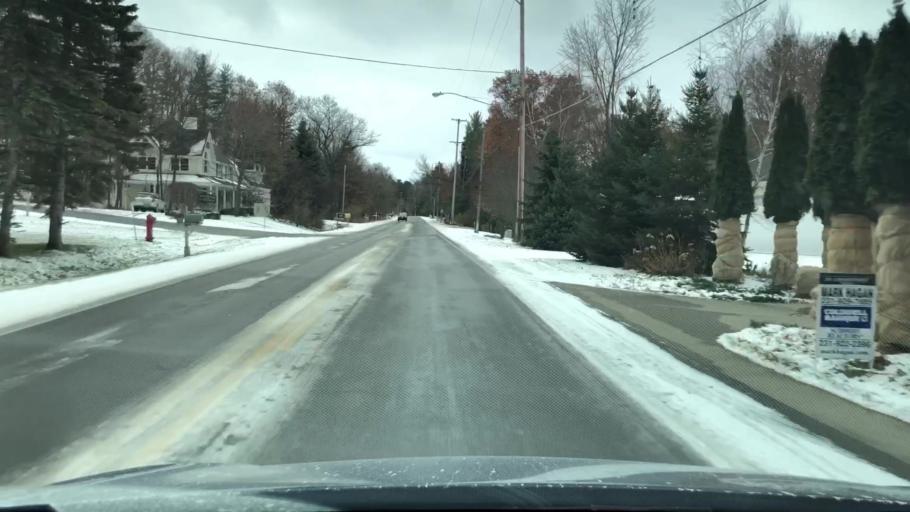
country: US
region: Michigan
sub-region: Grand Traverse County
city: Traverse City
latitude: 44.7813
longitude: -85.5900
